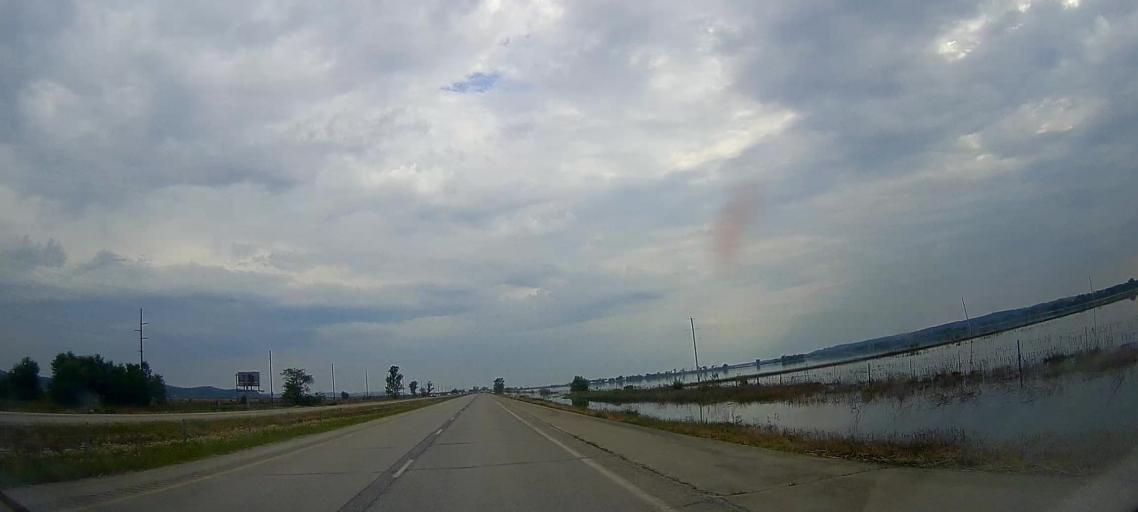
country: US
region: Iowa
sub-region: Harrison County
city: Missouri Valley
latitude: 41.4492
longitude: -95.8998
